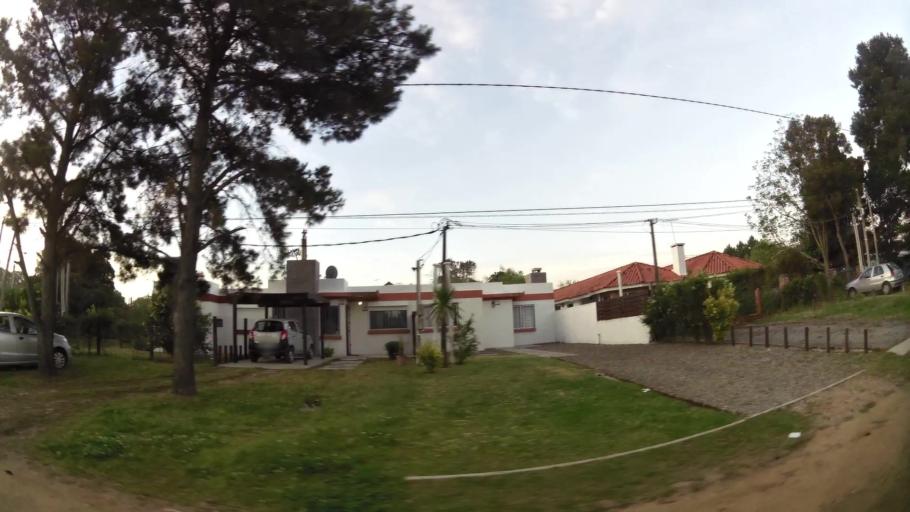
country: UY
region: Canelones
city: Atlantida
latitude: -34.7743
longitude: -55.7472
